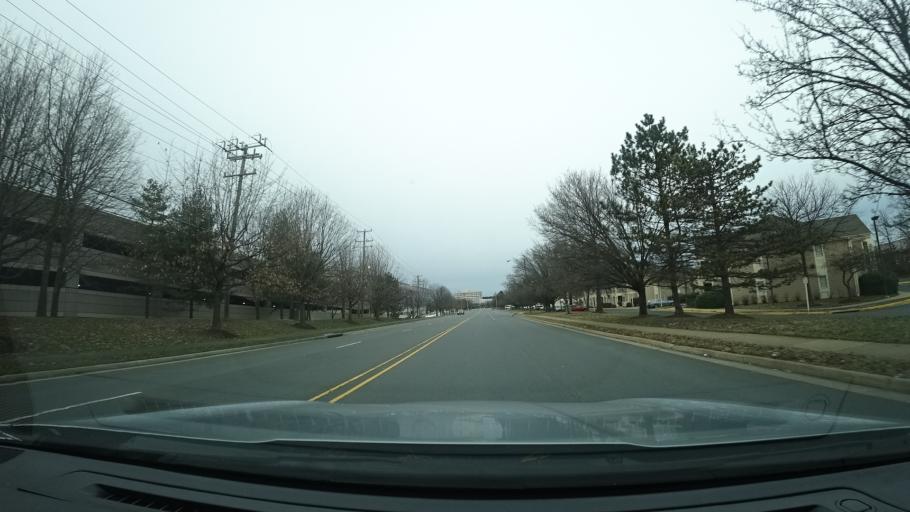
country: US
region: Virginia
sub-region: Fairfax County
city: Floris
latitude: 38.9503
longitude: -77.4191
